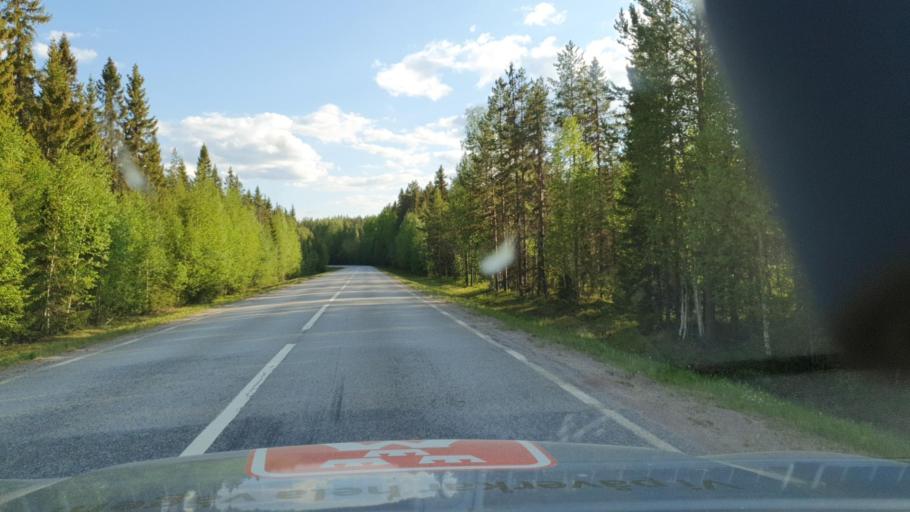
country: SE
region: Vaesternorrland
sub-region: Solleftea Kommun
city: As
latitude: 63.7332
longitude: 16.9881
